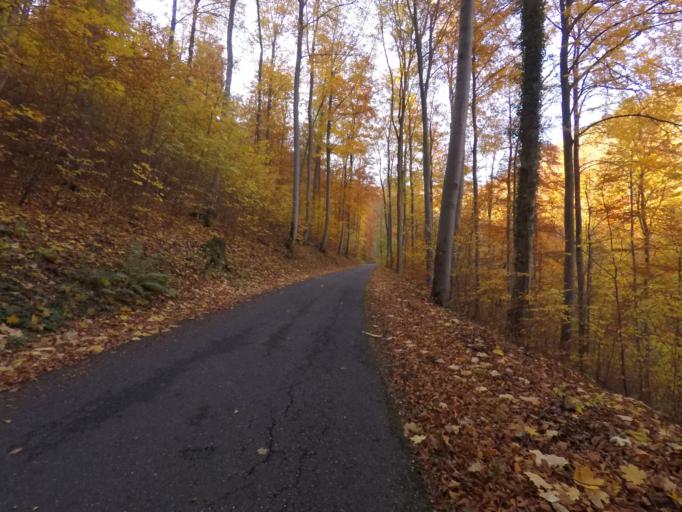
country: DE
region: Baden-Wuerttemberg
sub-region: Tuebingen Region
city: Pfullingen
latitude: 48.4371
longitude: 9.2351
